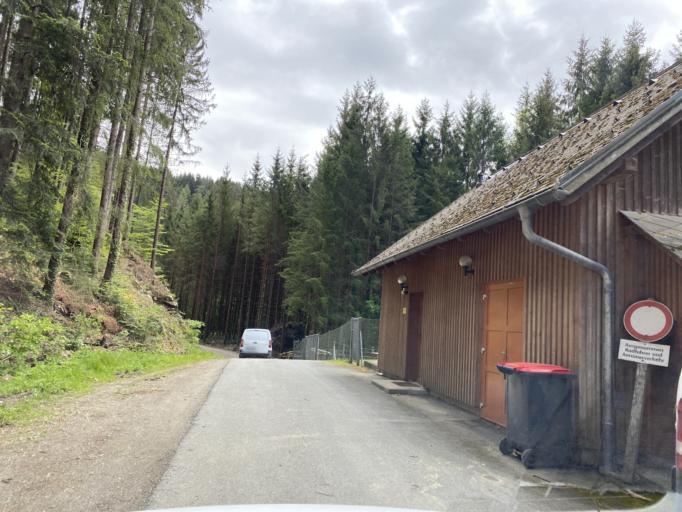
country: AT
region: Styria
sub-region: Politischer Bezirk Weiz
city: Koglhof
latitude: 47.3131
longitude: 15.6881
